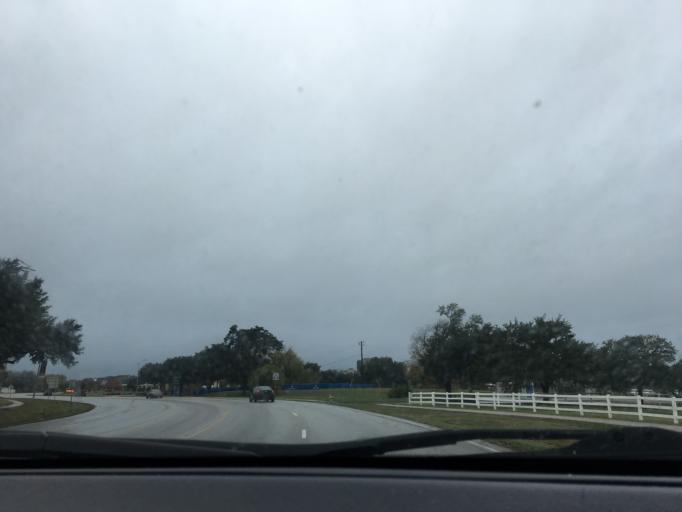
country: US
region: Texas
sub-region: Hays County
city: San Marcos
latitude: 29.8861
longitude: -97.9287
